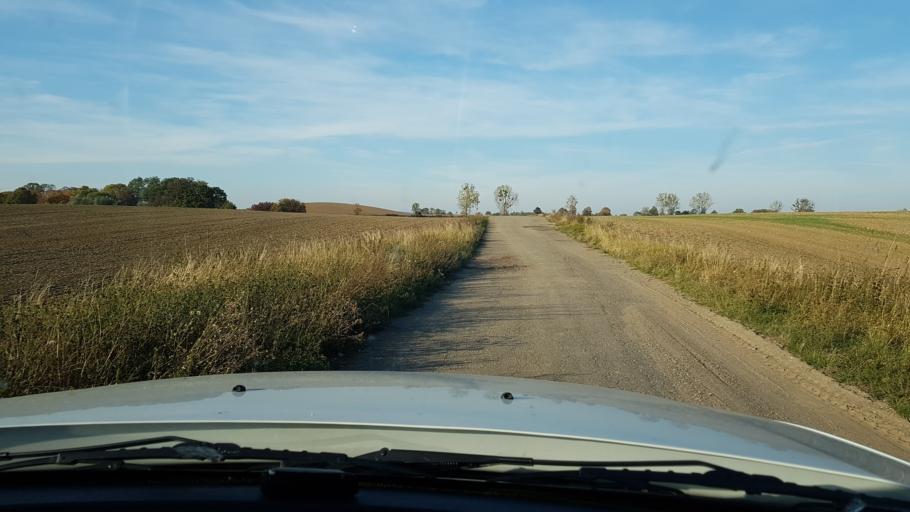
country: PL
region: West Pomeranian Voivodeship
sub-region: Powiat gryfinski
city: Moryn
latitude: 52.8929
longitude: 14.3094
